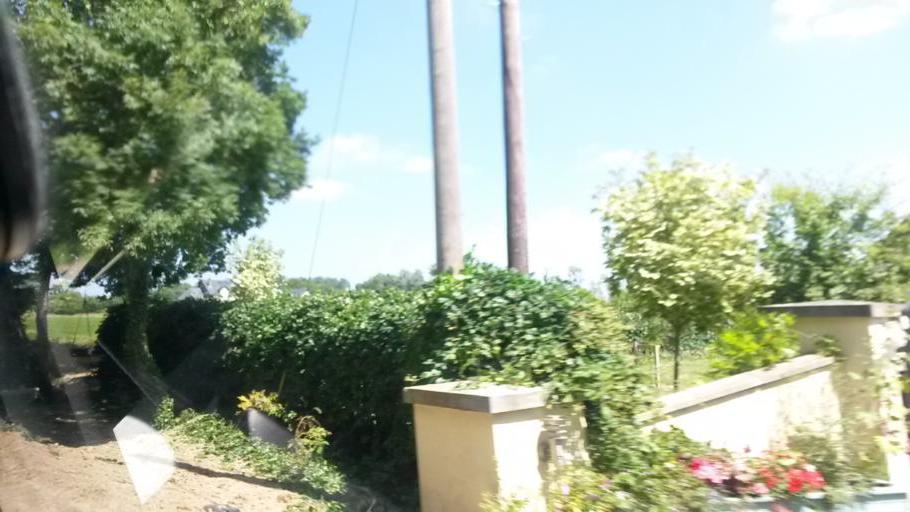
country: IE
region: Leinster
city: Balrothery
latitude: 53.5385
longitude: -6.2472
